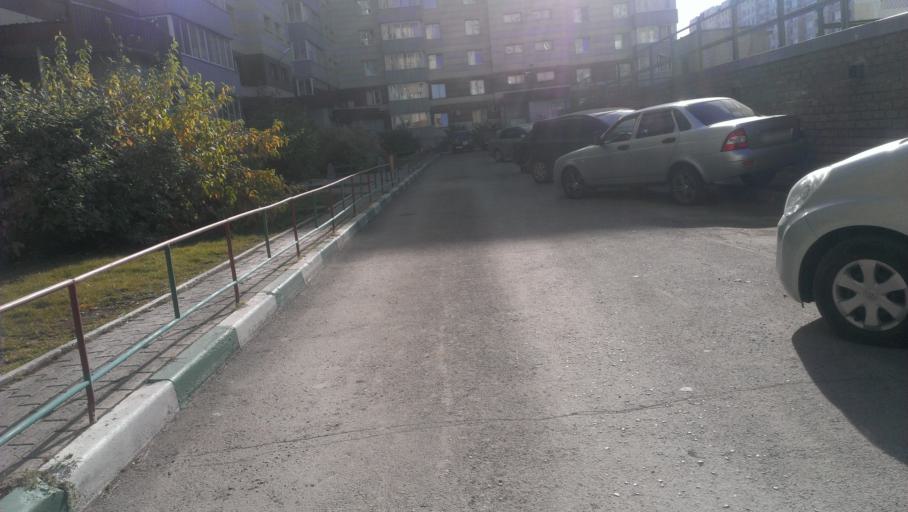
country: RU
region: Altai Krai
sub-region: Gorod Barnaulskiy
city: Barnaul
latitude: 53.3376
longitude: 83.6931
